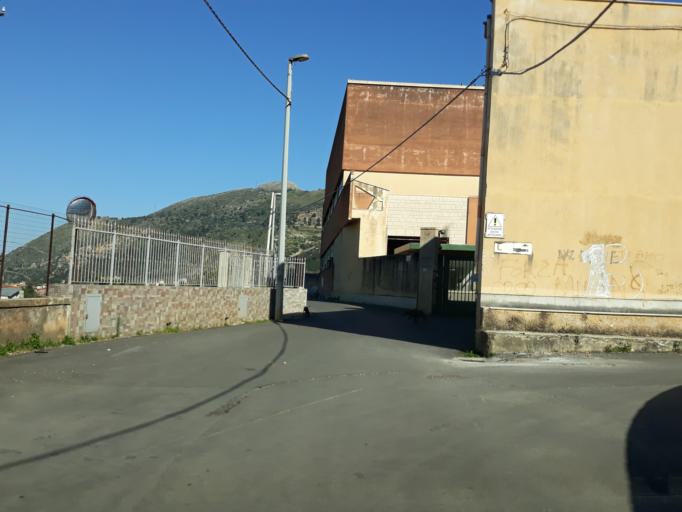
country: IT
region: Sicily
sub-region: Palermo
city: Villa Ciambra
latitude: 38.0753
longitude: 13.3574
